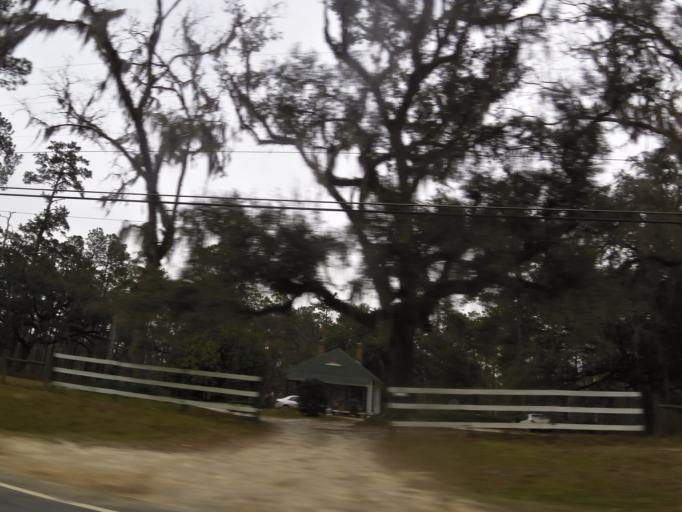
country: US
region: Georgia
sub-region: Thomas County
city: Thomasville
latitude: 30.8653
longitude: -84.0317
